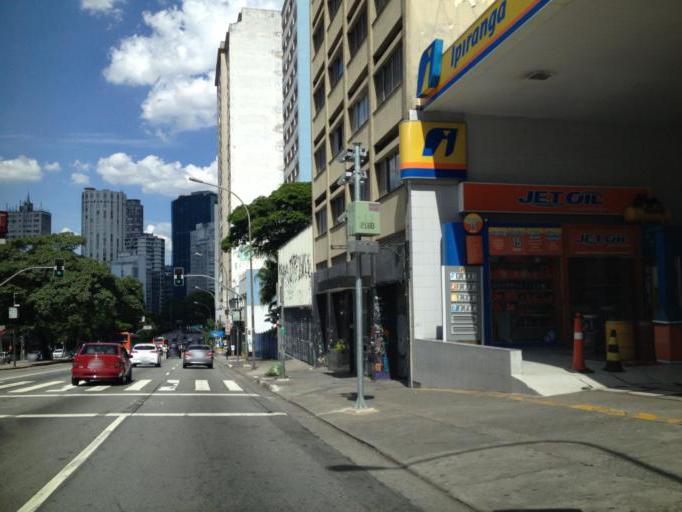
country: BR
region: Sao Paulo
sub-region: Sao Paulo
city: Sao Paulo
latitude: -23.5485
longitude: -46.6505
